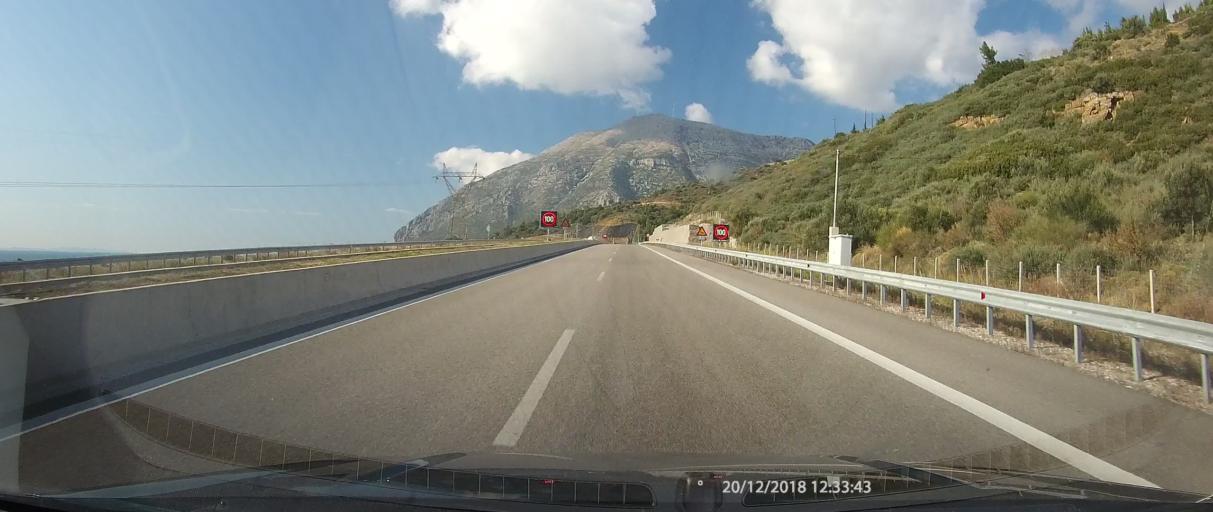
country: GR
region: West Greece
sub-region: Nomos Aitolias kai Akarnanias
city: Antirrio
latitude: 38.3520
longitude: 21.7335
